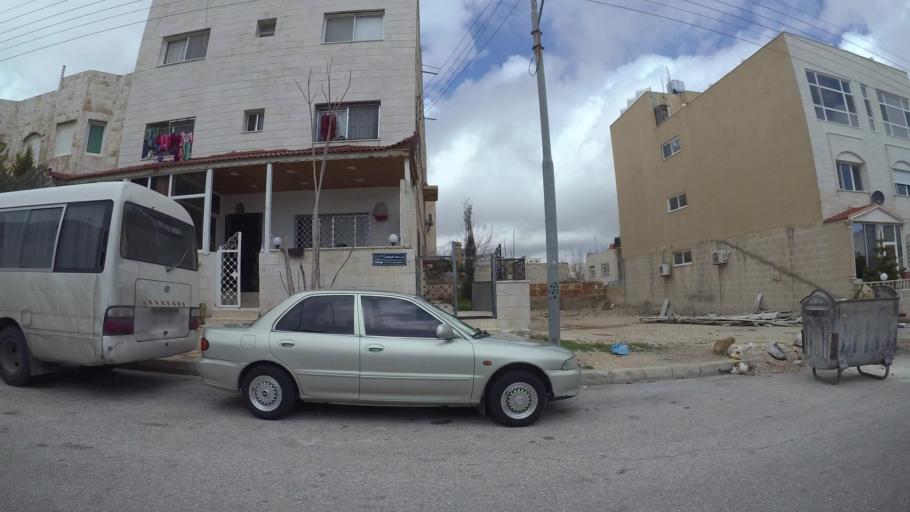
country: JO
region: Amman
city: Al Jubayhah
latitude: 32.0639
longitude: 35.8822
